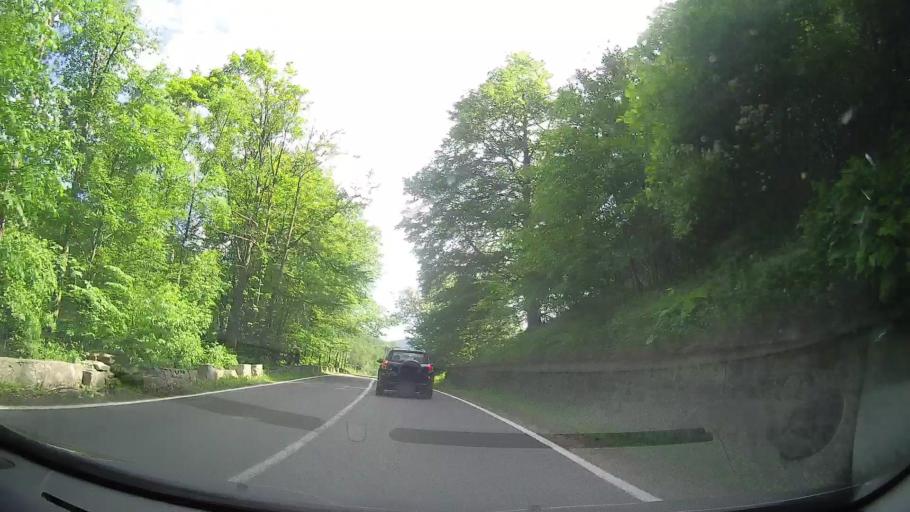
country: RO
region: Prahova
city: Maneciu
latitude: 45.3878
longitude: 25.9292
